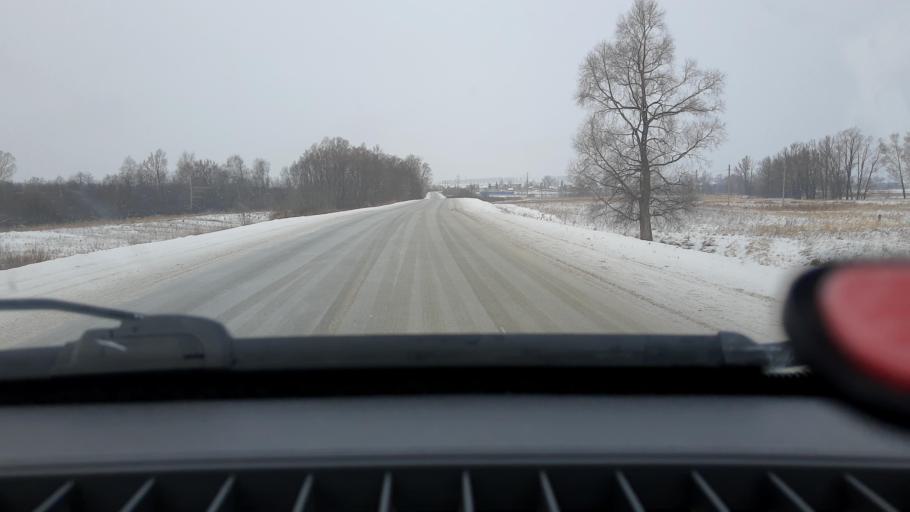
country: RU
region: Bashkortostan
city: Iglino
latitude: 54.7277
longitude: 56.4050
